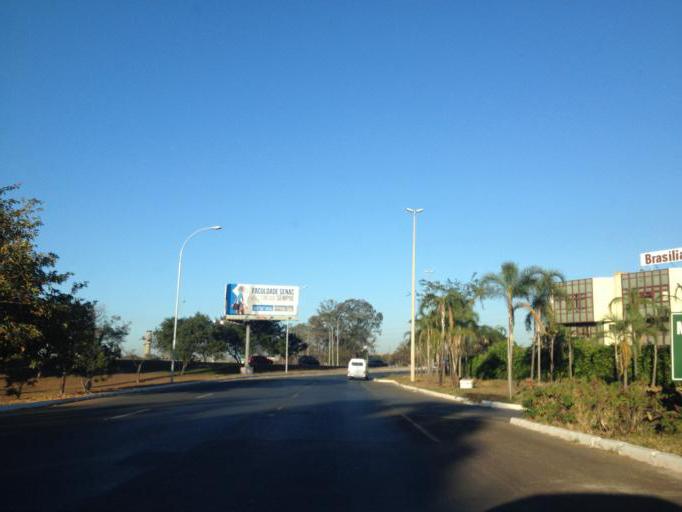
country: BR
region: Federal District
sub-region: Brasilia
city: Brasilia
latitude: -15.8070
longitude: -47.9490
